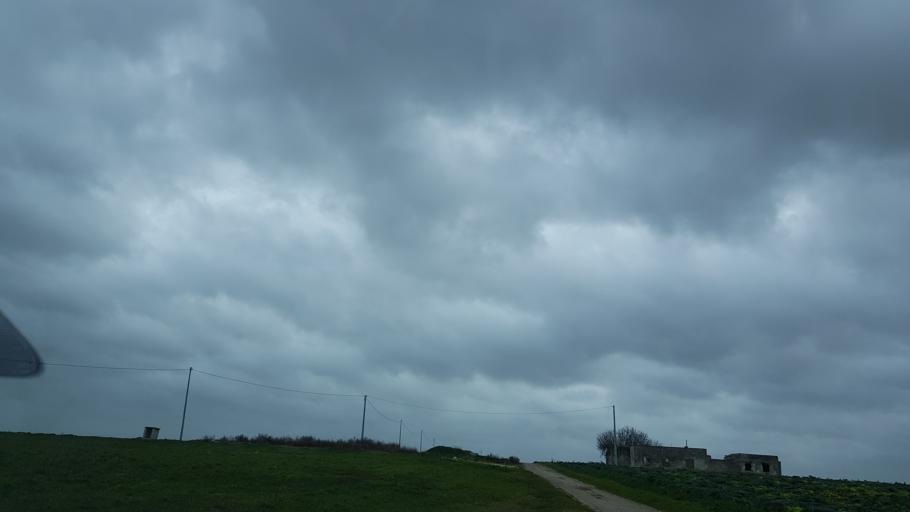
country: IT
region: Apulia
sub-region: Provincia di Brindisi
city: Brindisi
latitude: 40.6617
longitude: 17.8635
